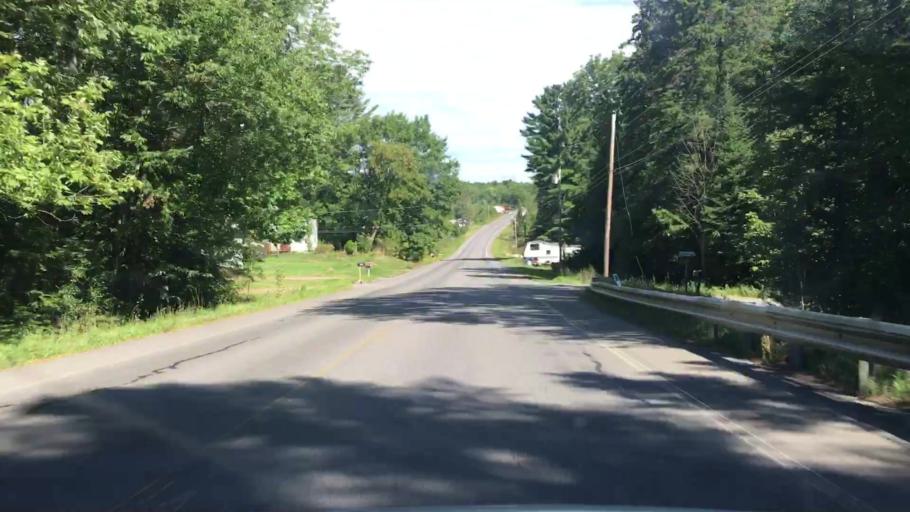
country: US
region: Maine
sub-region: Penobscot County
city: Dexter
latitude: 45.0779
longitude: -69.2309
